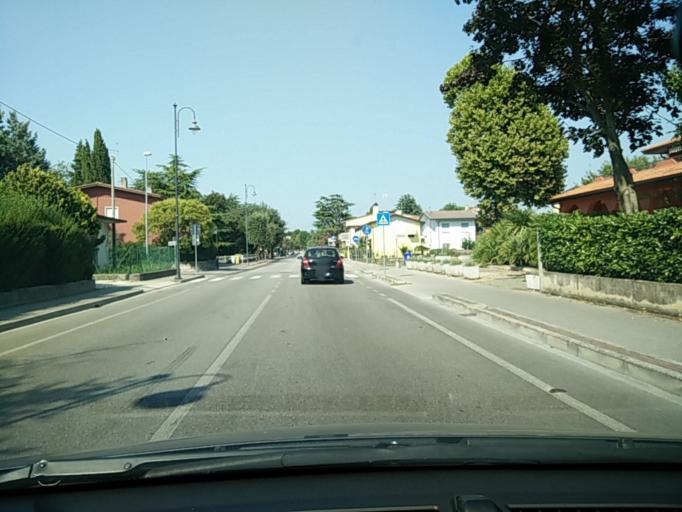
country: IT
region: Veneto
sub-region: Provincia di Venezia
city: San Giorgio di Livenza
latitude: 45.6493
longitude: 12.7956
